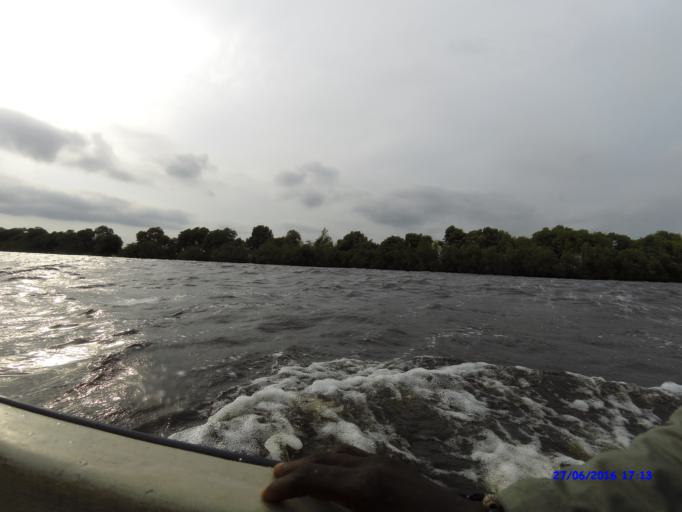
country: BJ
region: Atlantique
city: Allada
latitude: 6.6019
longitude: 1.9855
